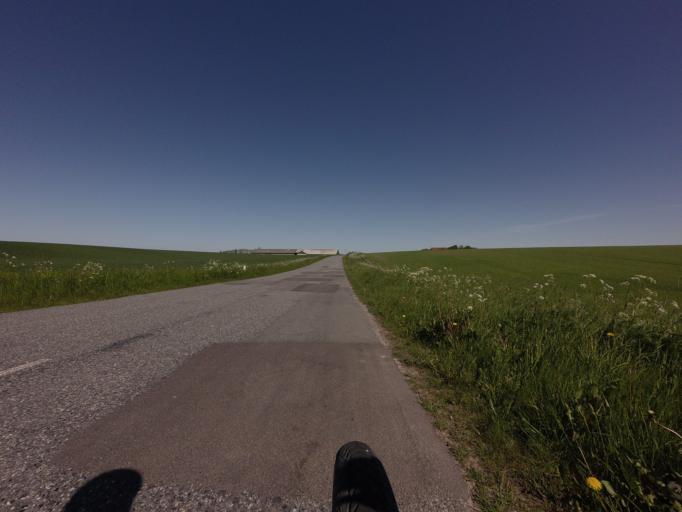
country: DK
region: North Denmark
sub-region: Hjorring Kommune
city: Hjorring
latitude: 57.4418
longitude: 9.8995
